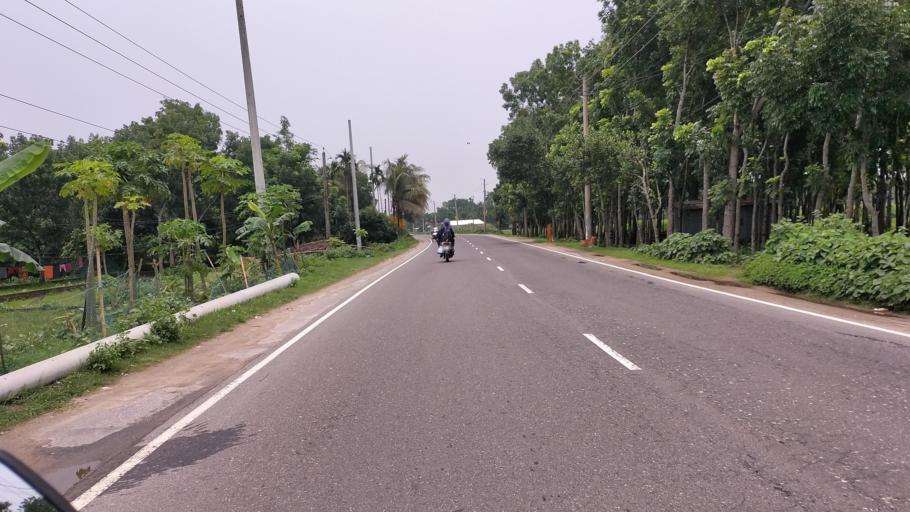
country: BD
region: Dhaka
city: Mymensingh
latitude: 24.7760
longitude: 90.4670
